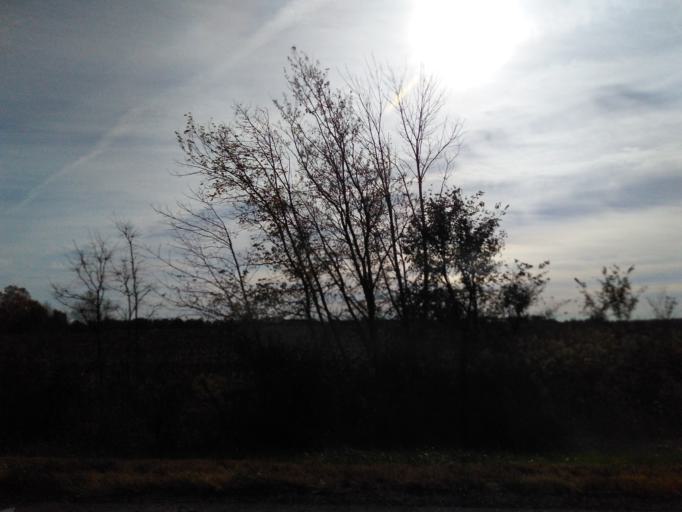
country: US
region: Illinois
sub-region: Madison County
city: Saint Jacob
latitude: 38.7721
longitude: -89.7471
